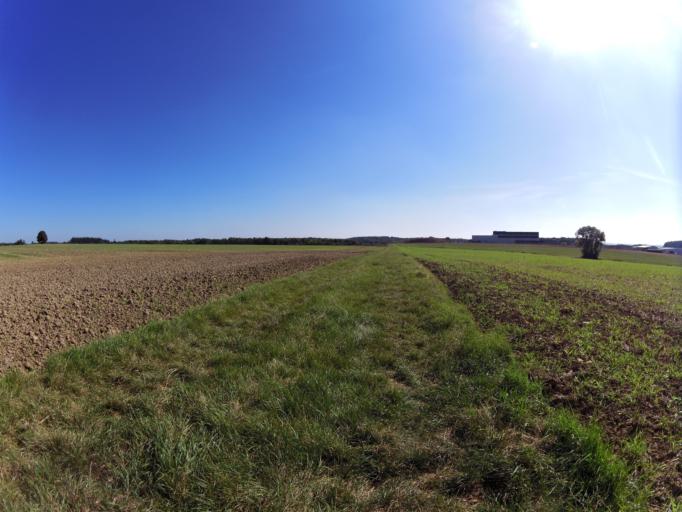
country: DE
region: Bavaria
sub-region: Regierungsbezirk Unterfranken
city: Kleinrinderfeld
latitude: 49.7022
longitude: 9.7896
